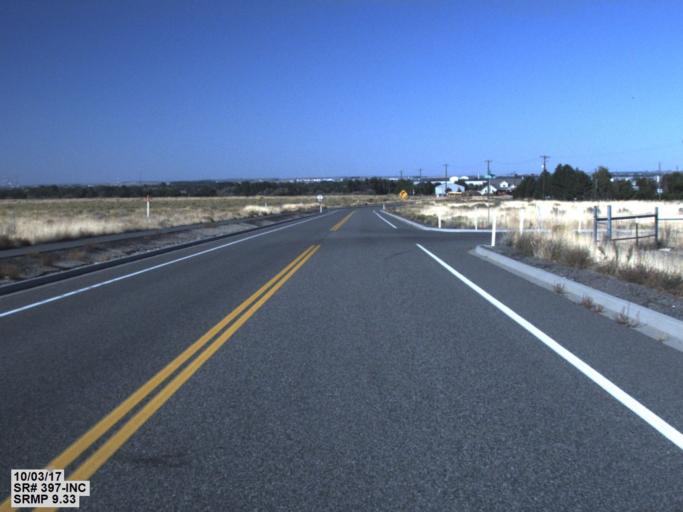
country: US
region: Washington
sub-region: Benton County
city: Finley
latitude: 46.1345
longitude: -119.0349
